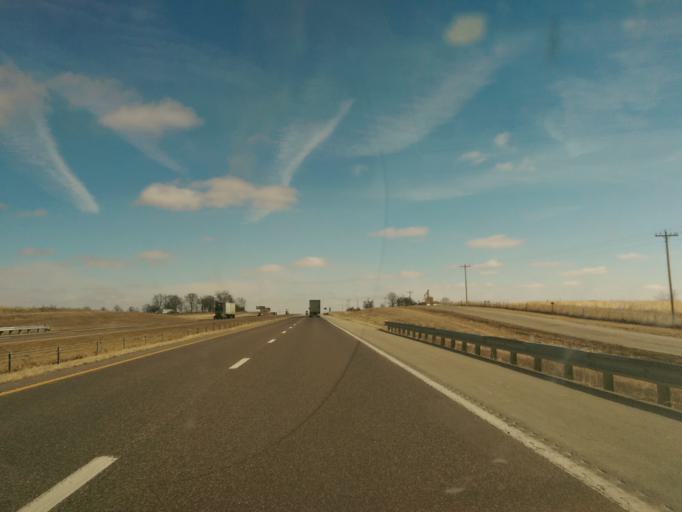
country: US
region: Missouri
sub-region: Callaway County
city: Fulton
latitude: 38.9439
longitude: -91.9077
